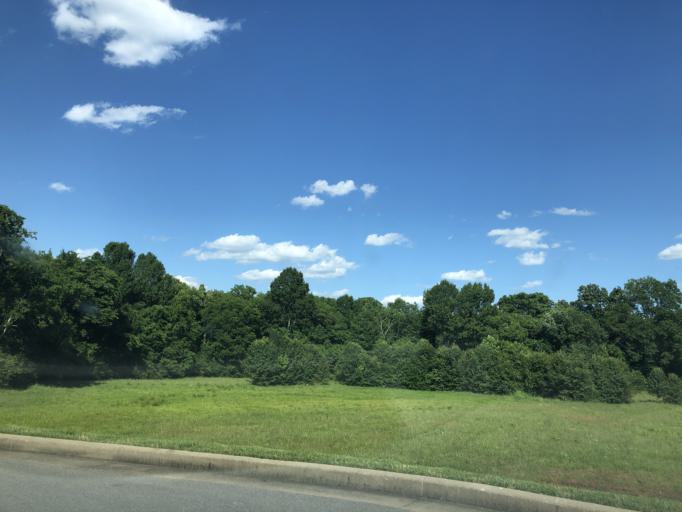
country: US
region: Tennessee
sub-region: Davidson County
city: Belle Meade
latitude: 36.0479
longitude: -86.9503
